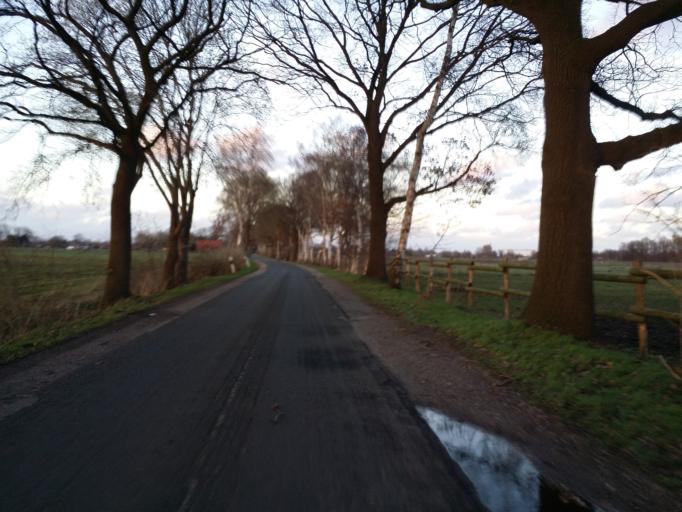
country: DE
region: Lower Saxony
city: Delmenhorst
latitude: 53.0130
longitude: 8.6164
